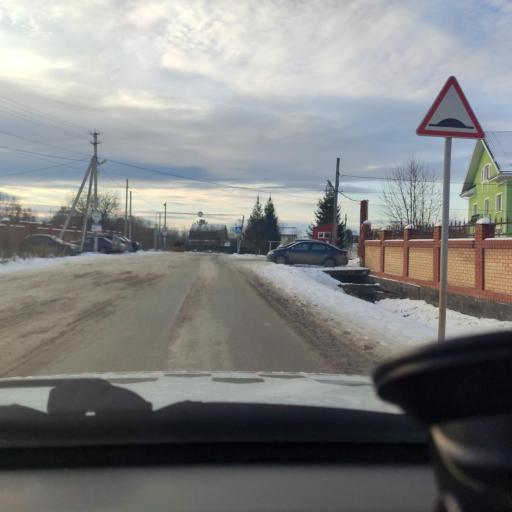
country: RU
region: Perm
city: Ferma
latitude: 57.9454
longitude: 56.3584
